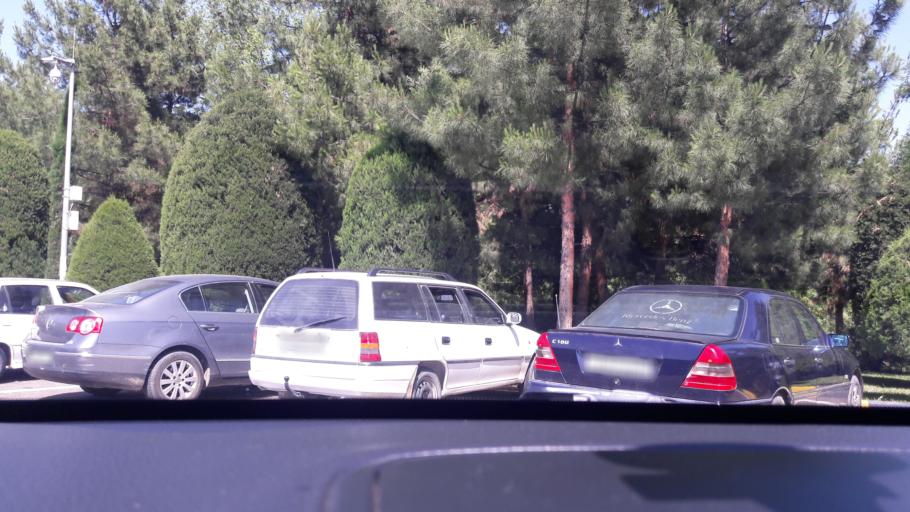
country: TJ
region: Dushanbe
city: Dushanbe
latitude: 38.5792
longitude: 68.8108
